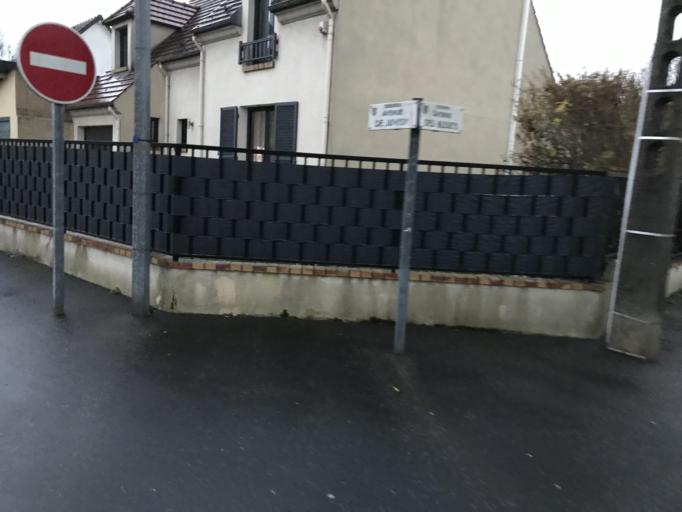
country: FR
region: Ile-de-France
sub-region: Departement de l'Essonne
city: Morangis
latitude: 48.7039
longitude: 2.3461
